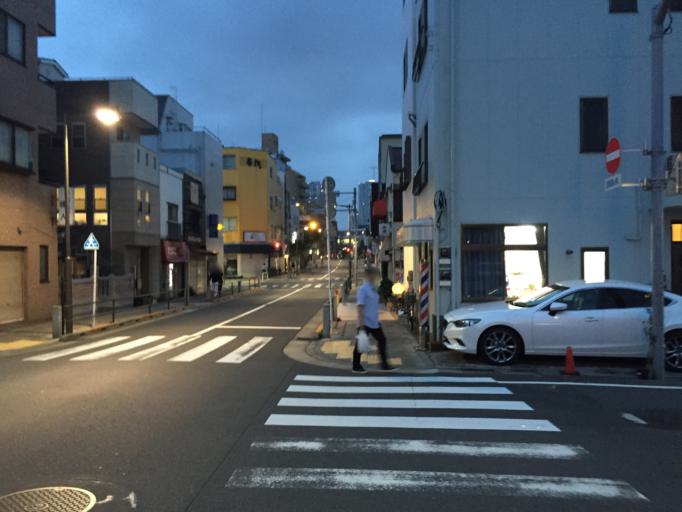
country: JP
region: Tokyo
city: Urayasu
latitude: 35.6697
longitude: 139.7977
